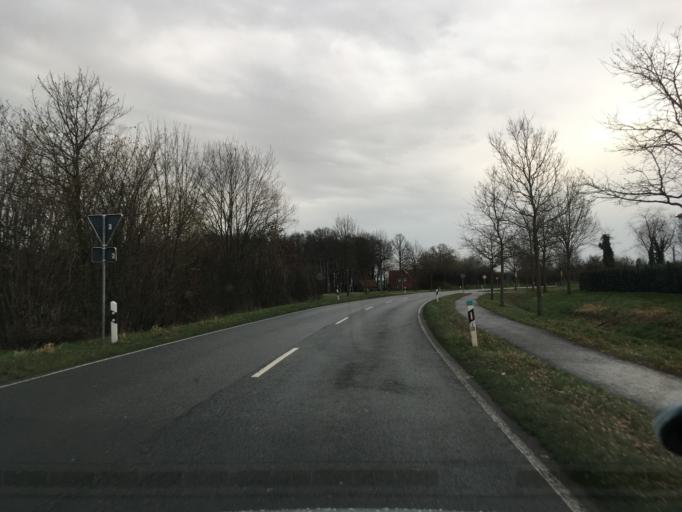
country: DE
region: North Rhine-Westphalia
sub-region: Regierungsbezirk Munster
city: Schoppingen
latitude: 52.0975
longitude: 7.2226
